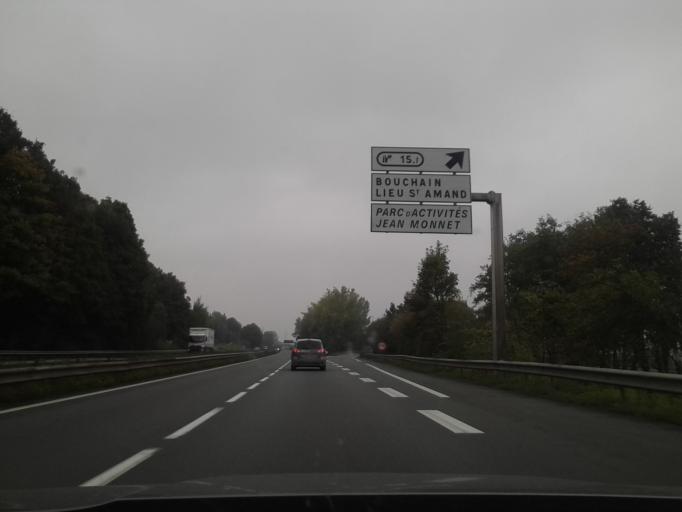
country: FR
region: Nord-Pas-de-Calais
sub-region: Departement du Nord
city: Lieu-Saint-Amand
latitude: 50.2714
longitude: 3.3347
